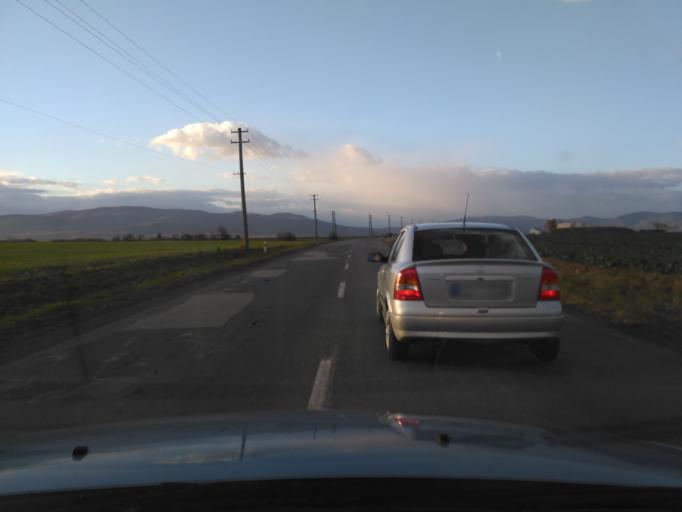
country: SK
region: Kosicky
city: Secovce
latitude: 48.6584
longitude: 21.6671
